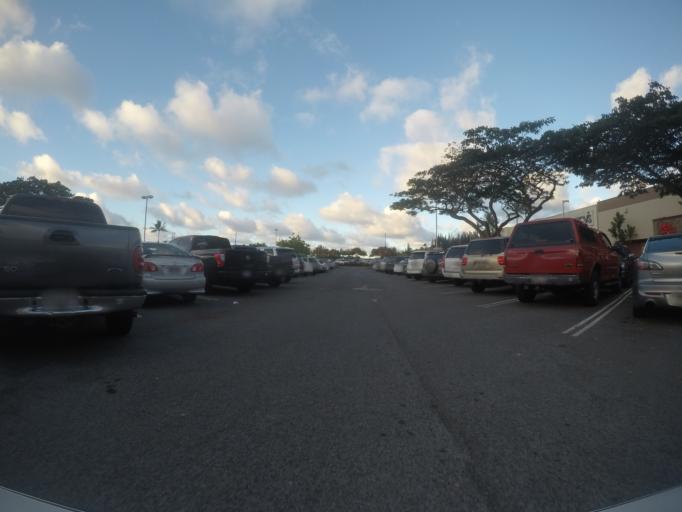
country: US
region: Hawaii
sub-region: Honolulu County
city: He'eia
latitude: 21.4207
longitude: -157.8053
